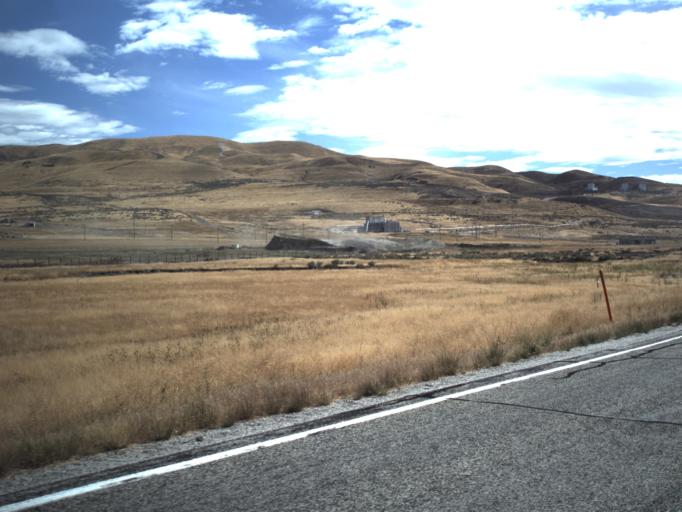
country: US
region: Utah
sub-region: Box Elder County
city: Tremonton
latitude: 41.6980
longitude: -112.4462
